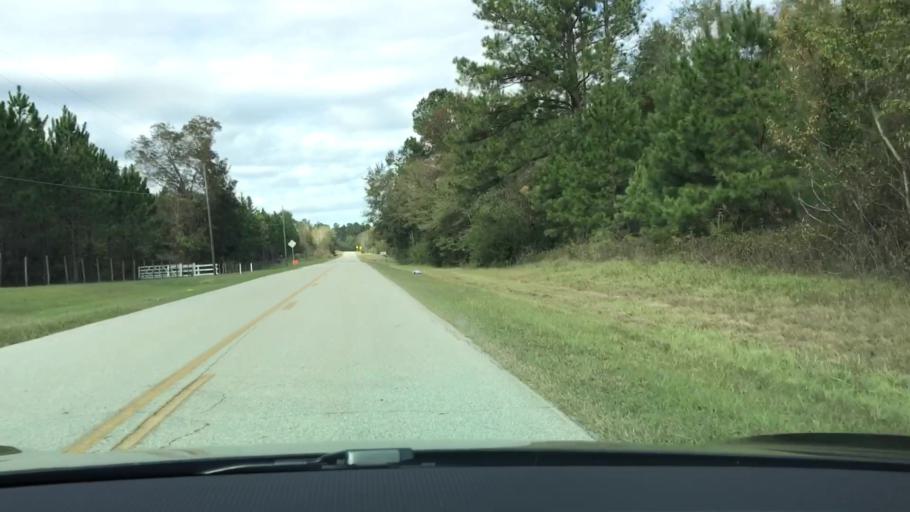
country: US
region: Georgia
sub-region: Jefferson County
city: Wadley
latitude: 32.7995
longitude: -82.3803
